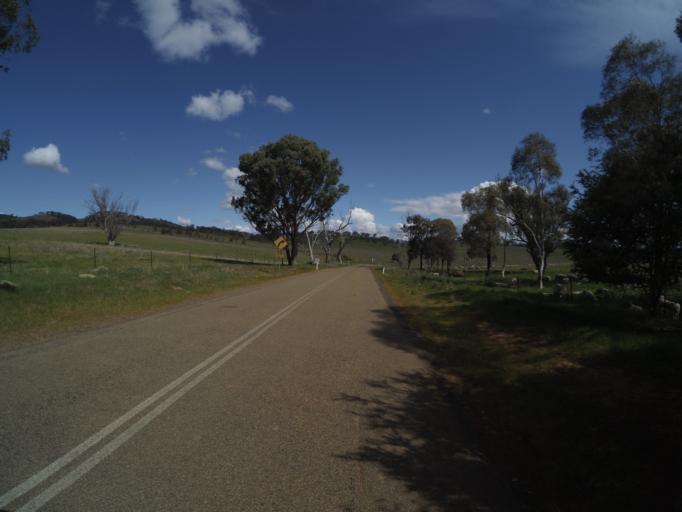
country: AU
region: New South Wales
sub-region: Yass Valley
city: Murrumbateman
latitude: -35.0205
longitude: 148.8525
